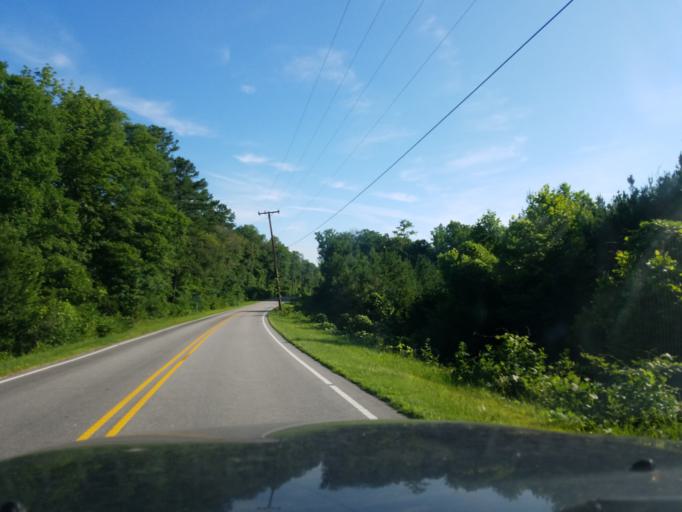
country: US
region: North Carolina
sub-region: Granville County
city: Butner
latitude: 36.1478
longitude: -78.7690
